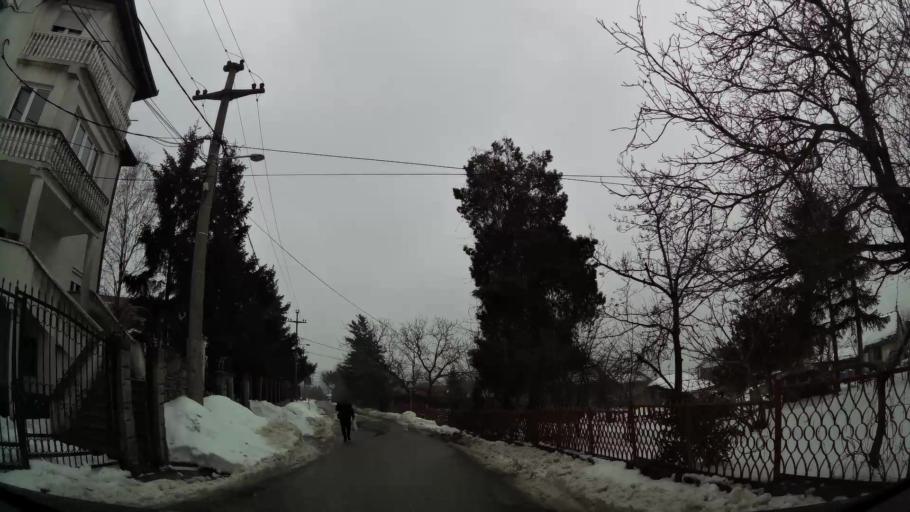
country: RS
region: Central Serbia
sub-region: Belgrade
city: Zvezdara
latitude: 44.7465
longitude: 20.5214
